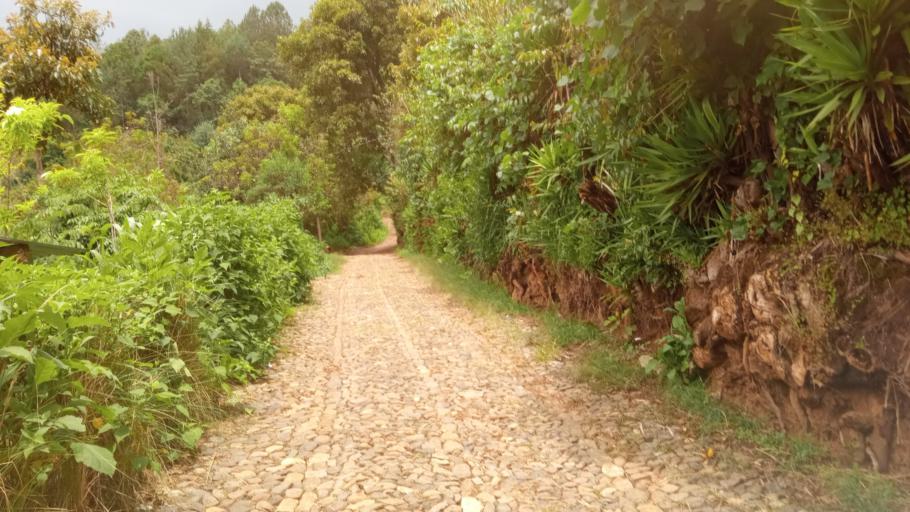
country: GT
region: San Marcos
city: Tejutla
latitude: 15.1164
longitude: -91.8055
